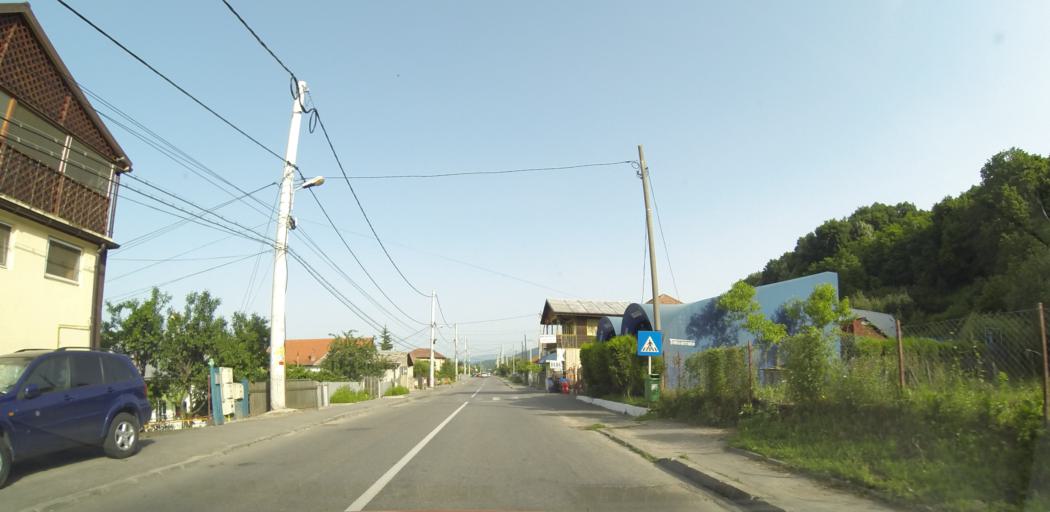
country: RO
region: Valcea
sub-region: Comuna Vladesti
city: Vladesti
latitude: 45.1118
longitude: 24.3258
